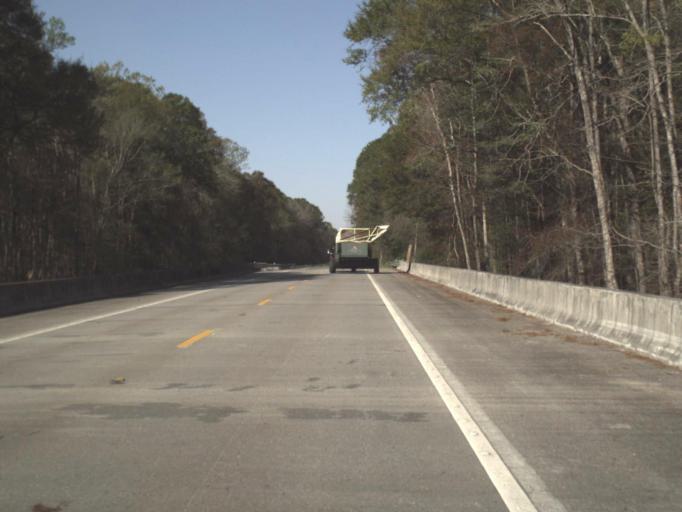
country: US
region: Florida
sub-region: Jackson County
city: Malone
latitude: 30.9474
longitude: -85.2588
